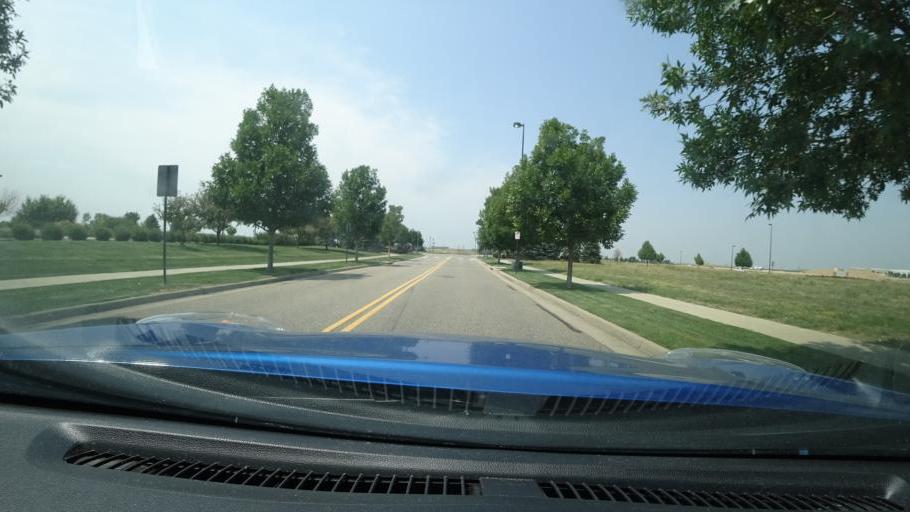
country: US
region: Colorado
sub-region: Adams County
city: Aurora
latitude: 39.7652
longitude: -104.7805
